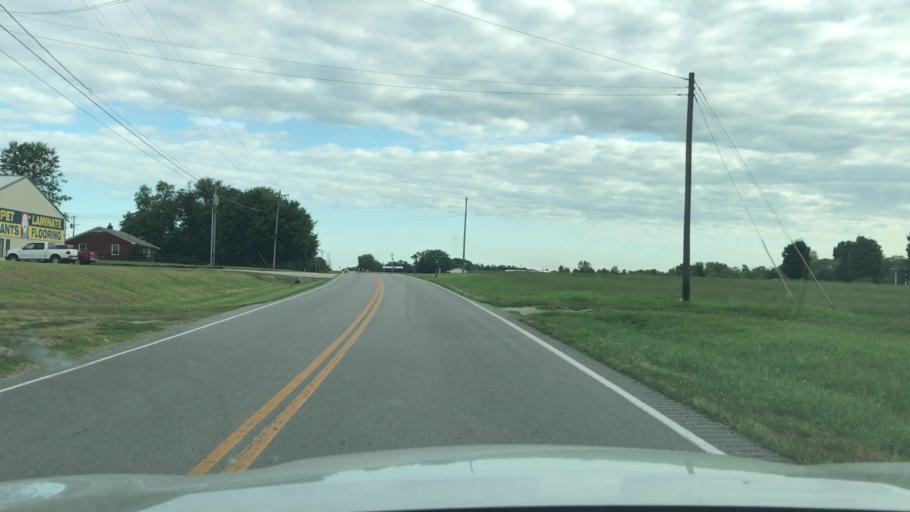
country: US
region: Kentucky
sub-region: Todd County
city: Elkton
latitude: 36.7818
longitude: -87.1635
